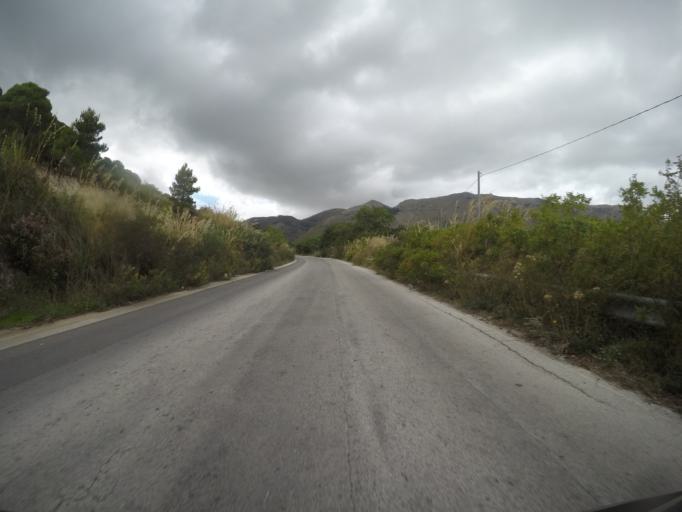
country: IT
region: Sicily
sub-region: Palermo
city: Montelepre
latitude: 38.1189
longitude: 13.1752
